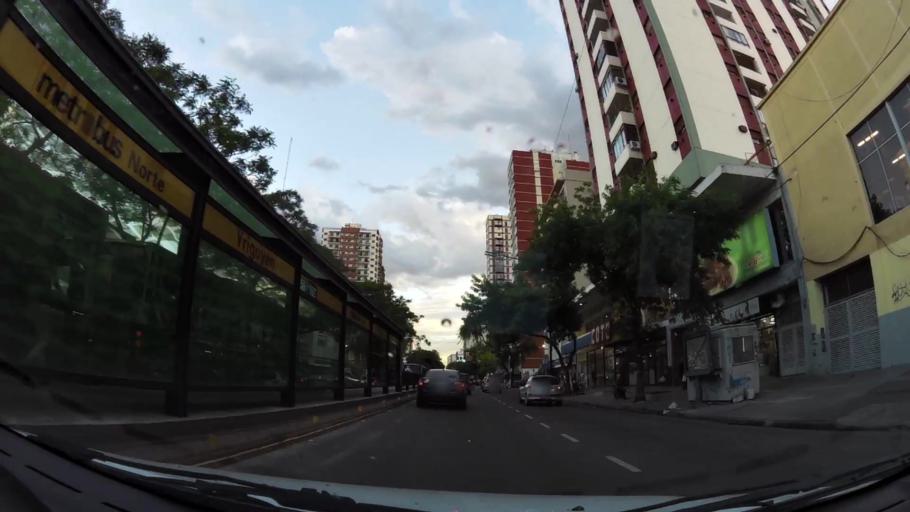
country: AR
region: Buenos Aires
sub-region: Partido de Vicente Lopez
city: Olivos
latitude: -34.5215
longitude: -58.4852
